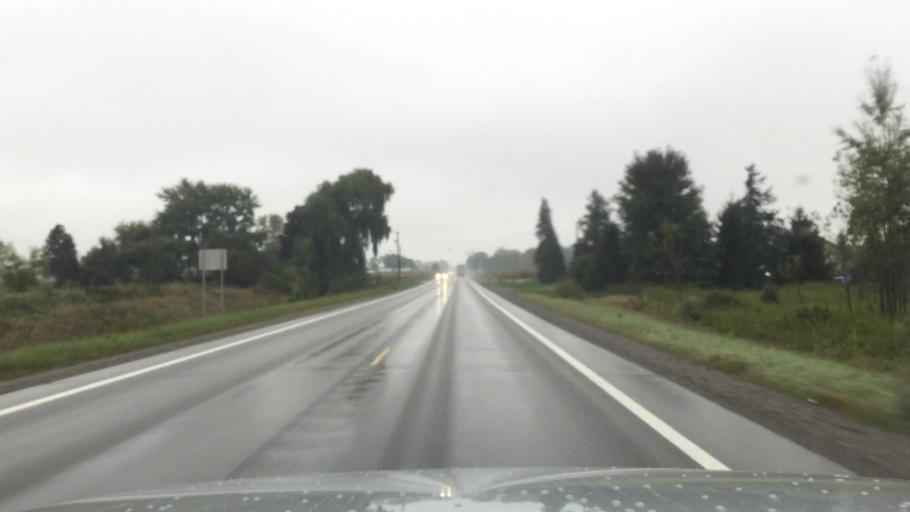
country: US
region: Michigan
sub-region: Saginaw County
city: Saginaw
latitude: 43.3600
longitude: -83.9547
